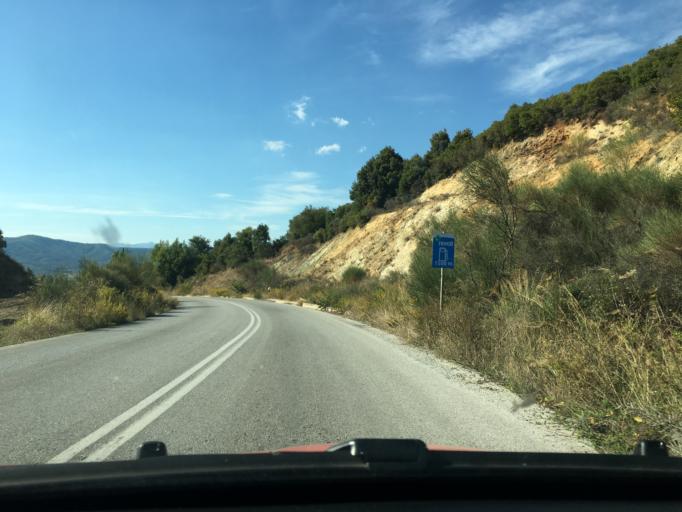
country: GR
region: Central Macedonia
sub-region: Nomos Chalkidikis
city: Ierissos
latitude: 40.3899
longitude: 23.8112
